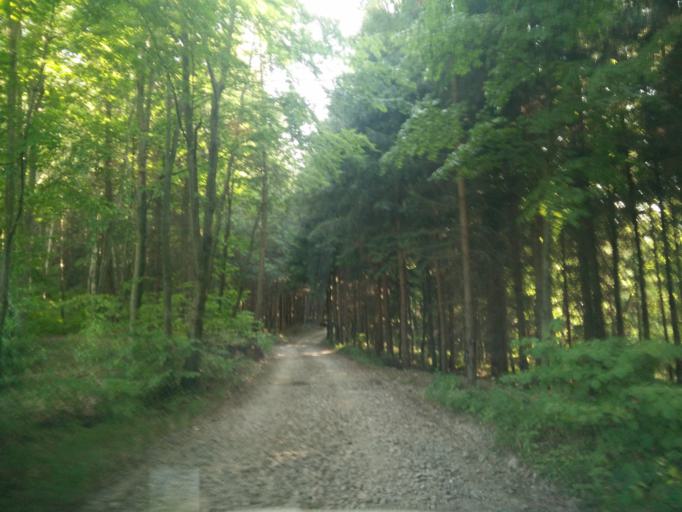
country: SK
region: Nitriansky
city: Prievidza
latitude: 48.7405
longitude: 18.6894
